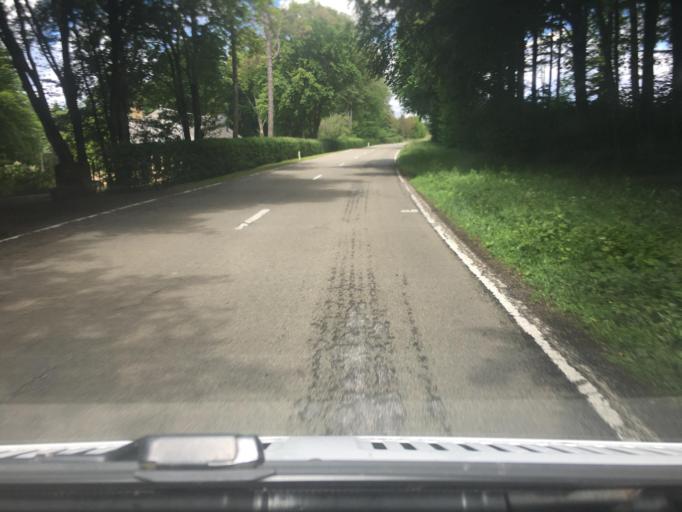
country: BE
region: Wallonia
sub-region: Province du Luxembourg
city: Florenville
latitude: 49.6478
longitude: 5.3397
